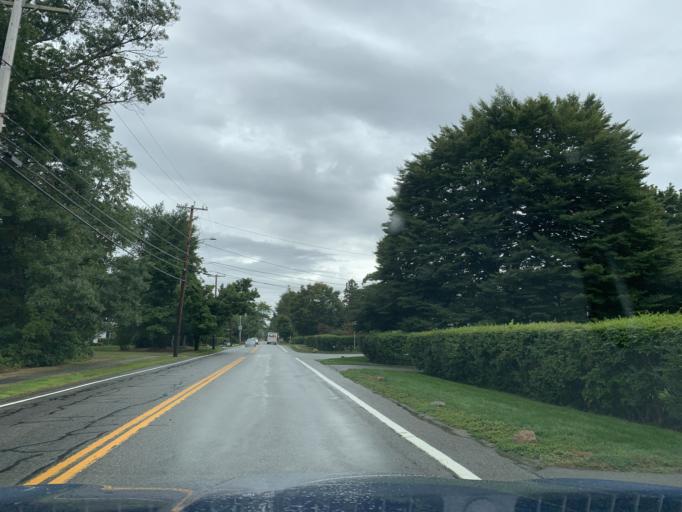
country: US
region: Rhode Island
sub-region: Bristol County
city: Barrington
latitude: 41.7341
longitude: -71.3029
